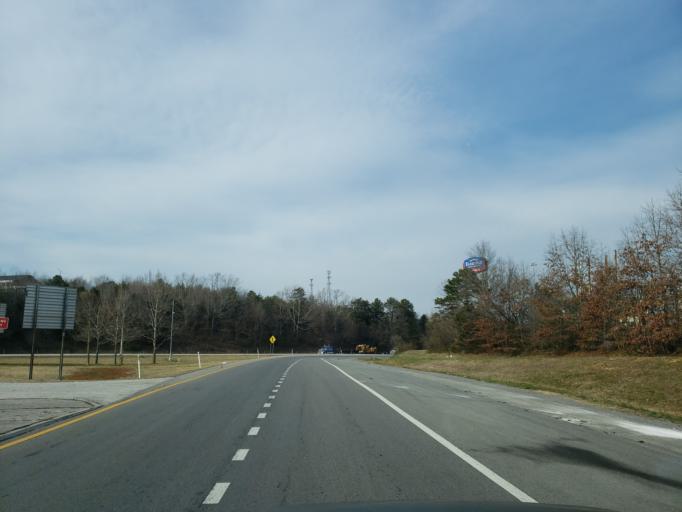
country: US
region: Tennessee
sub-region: Bradley County
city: Cleveland
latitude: 35.1937
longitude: -84.8850
